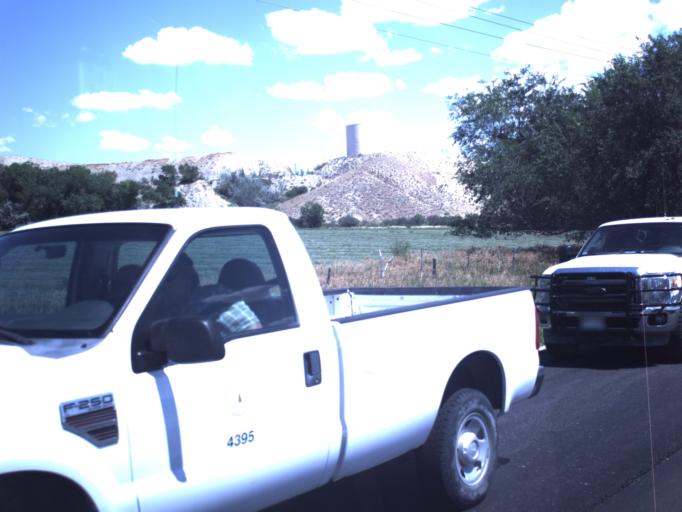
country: US
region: Utah
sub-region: Emery County
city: Orangeville
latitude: 39.2408
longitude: -111.0604
